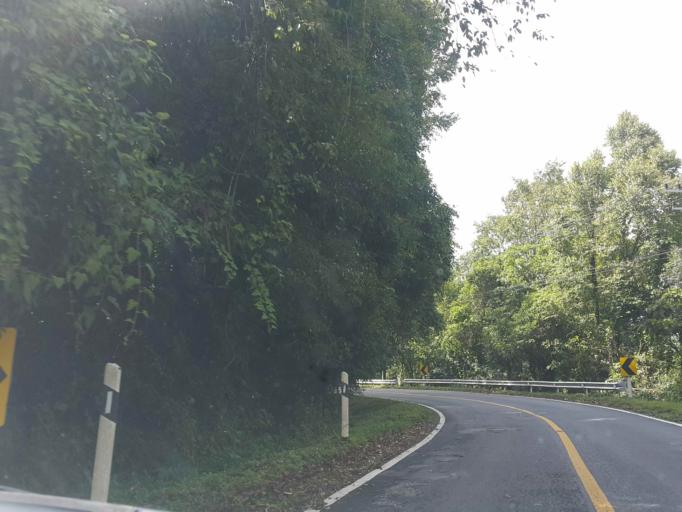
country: TH
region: Chiang Mai
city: Mae Chaem
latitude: 18.5454
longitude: 98.4873
